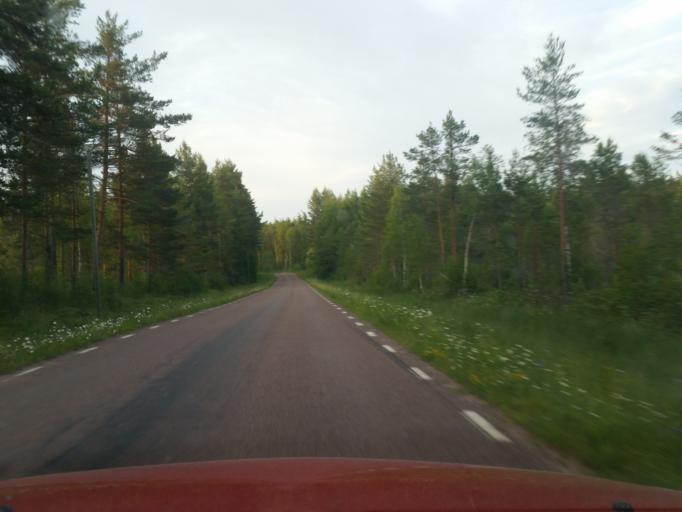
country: SE
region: Dalarna
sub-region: Gagnefs Kommun
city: Gagnef
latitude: 60.6723
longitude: 15.1686
